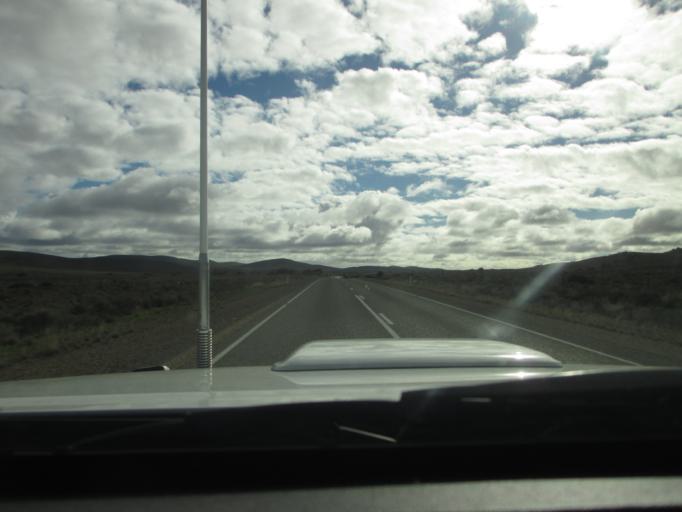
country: AU
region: South Australia
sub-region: Flinders Ranges
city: Quorn
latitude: -32.2394
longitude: 138.5130
